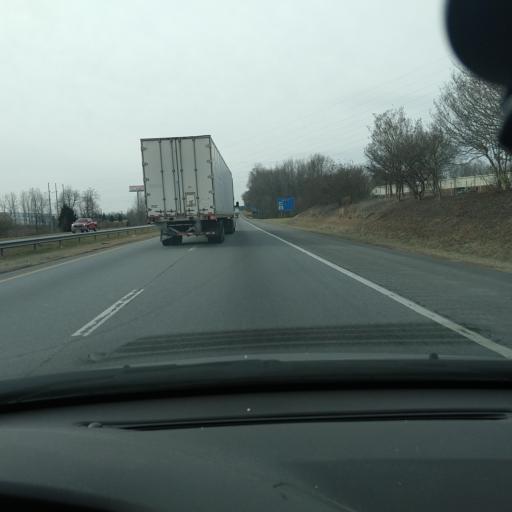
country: US
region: North Carolina
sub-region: Cleveland County
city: Kings Mountain
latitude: 35.2323
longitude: -81.3221
